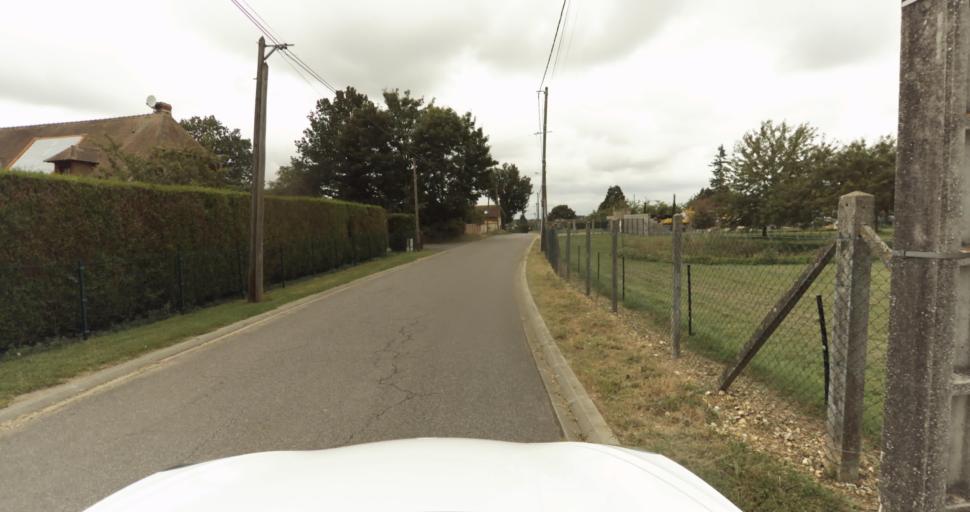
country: FR
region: Haute-Normandie
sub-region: Departement de l'Eure
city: Saint-Sebastien-de-Morsent
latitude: 49.0079
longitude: 1.0649
